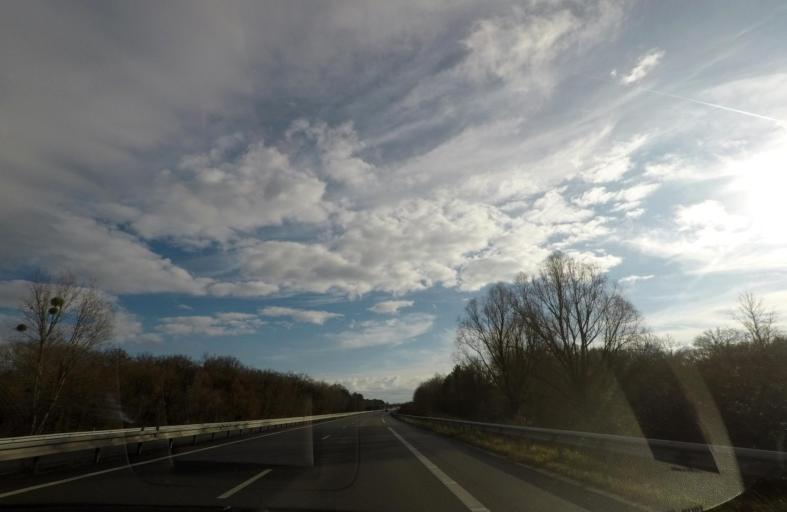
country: FR
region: Centre
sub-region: Departement du Loir-et-Cher
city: Chatres-sur-Cher
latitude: 47.3059
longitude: 1.8525
